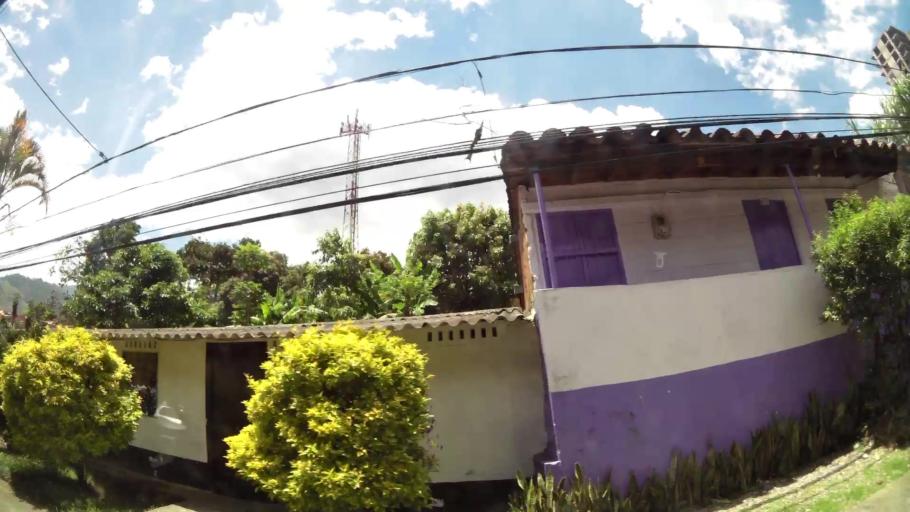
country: CO
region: Antioquia
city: La Estrella
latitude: 6.1553
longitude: -75.6382
